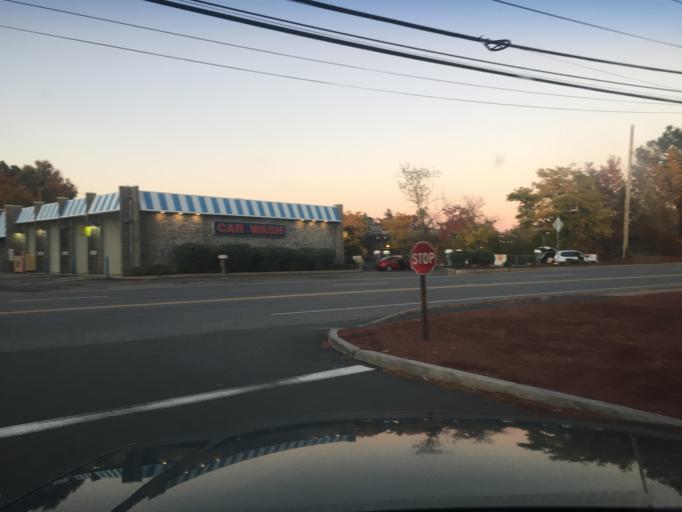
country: US
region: Massachusetts
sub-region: Worcester County
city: Milford
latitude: 42.1501
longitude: -71.5025
